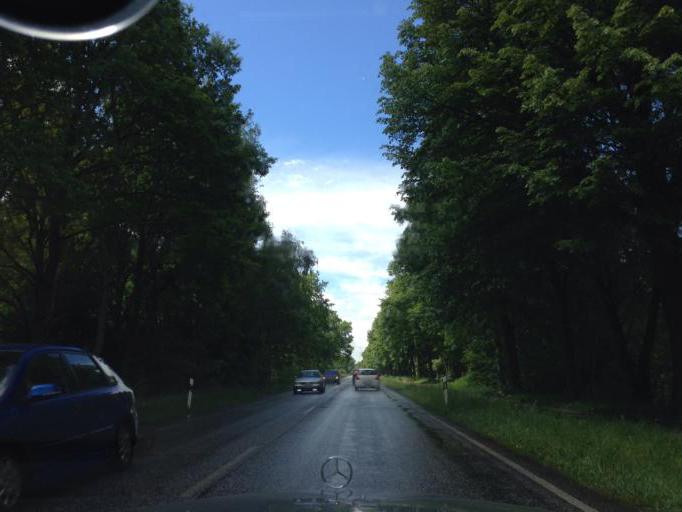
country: DE
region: Hamburg
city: Langenhorn
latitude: 53.7040
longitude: 10.0206
